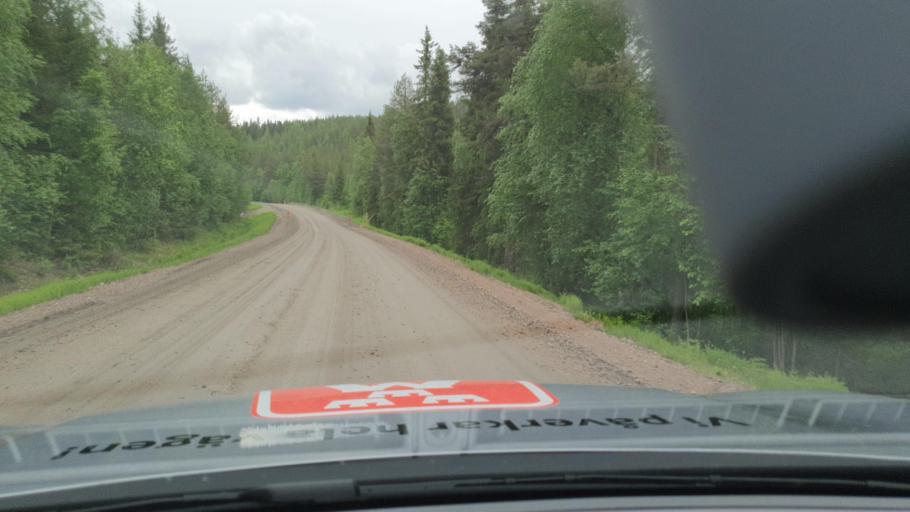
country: SE
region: Norrbotten
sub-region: Overtornea Kommun
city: OEvertornea
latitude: 66.4227
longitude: 23.5454
